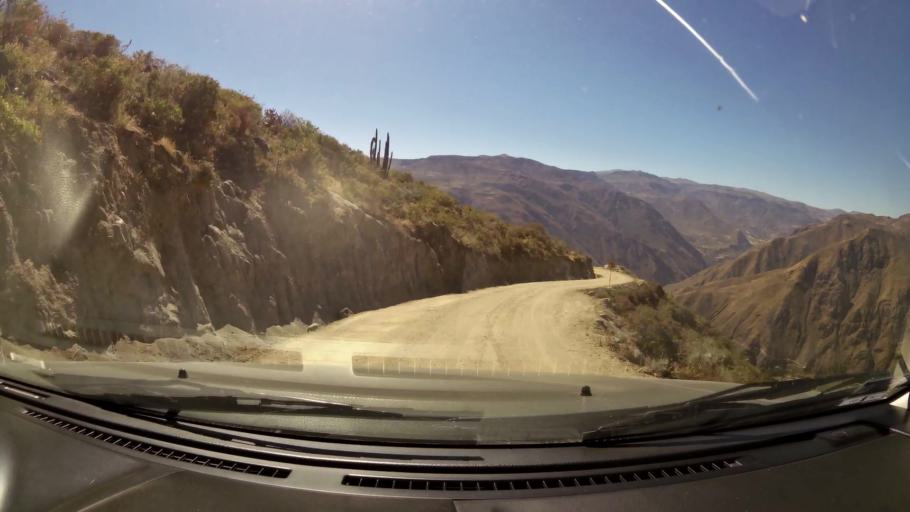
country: PE
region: Huancavelica
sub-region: Huaytara
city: Quito-Arma
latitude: -13.6157
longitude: -75.3514
